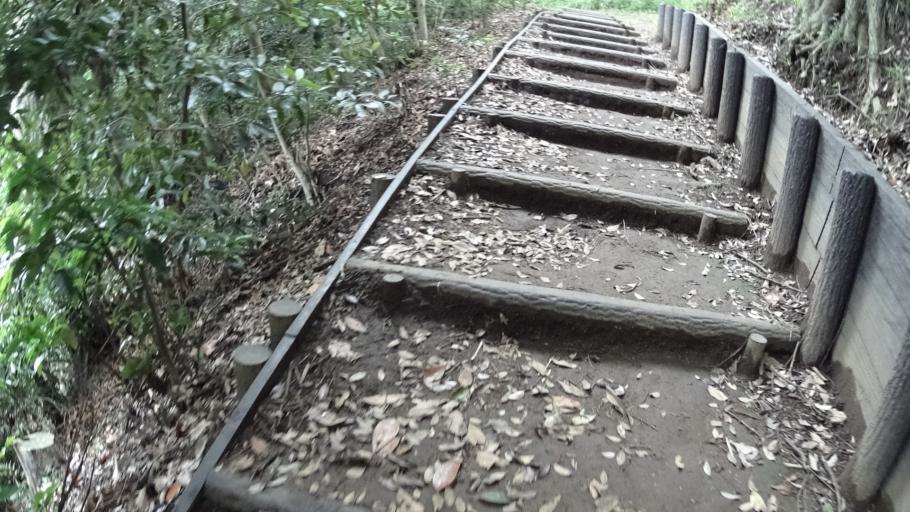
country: JP
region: Kanagawa
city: Zushi
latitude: 35.3574
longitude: 139.6077
